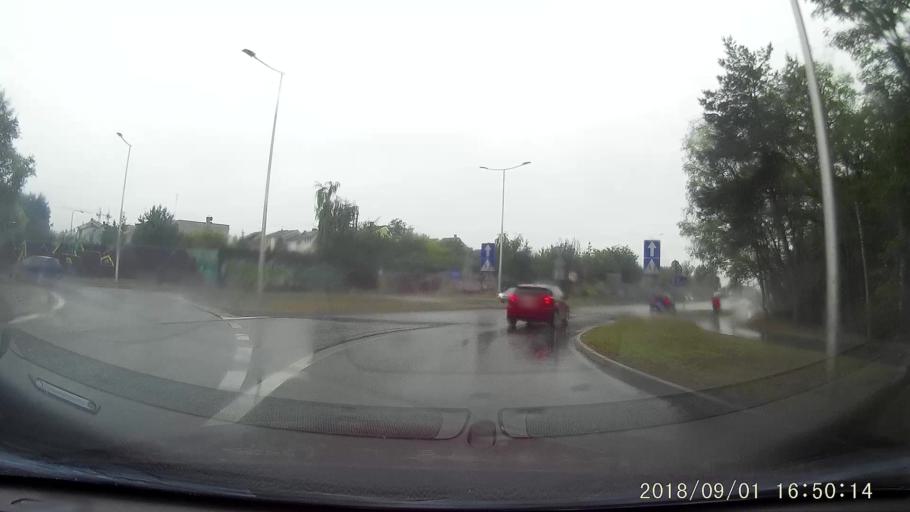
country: PL
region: Lubusz
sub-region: Zielona Gora
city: Zielona Gora
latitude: 51.9607
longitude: 15.5071
